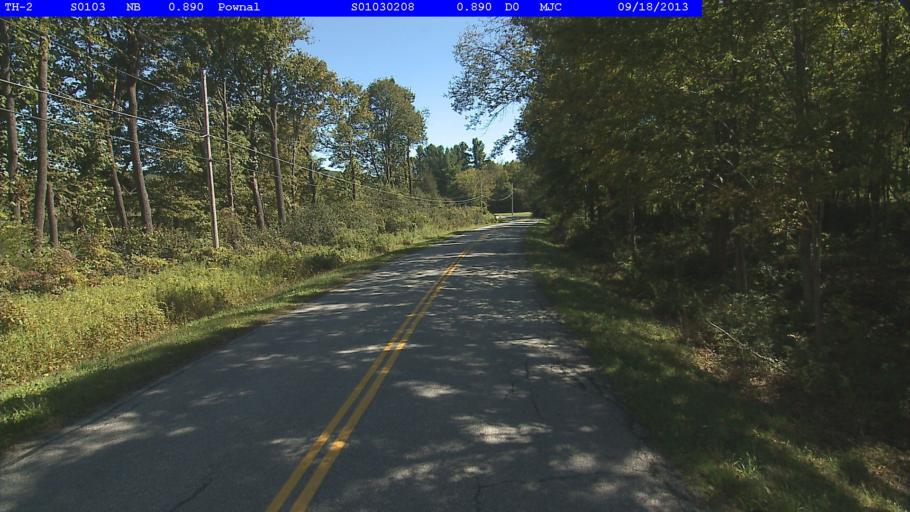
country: US
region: Vermont
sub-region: Bennington County
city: Bennington
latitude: 42.8021
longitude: -73.2526
